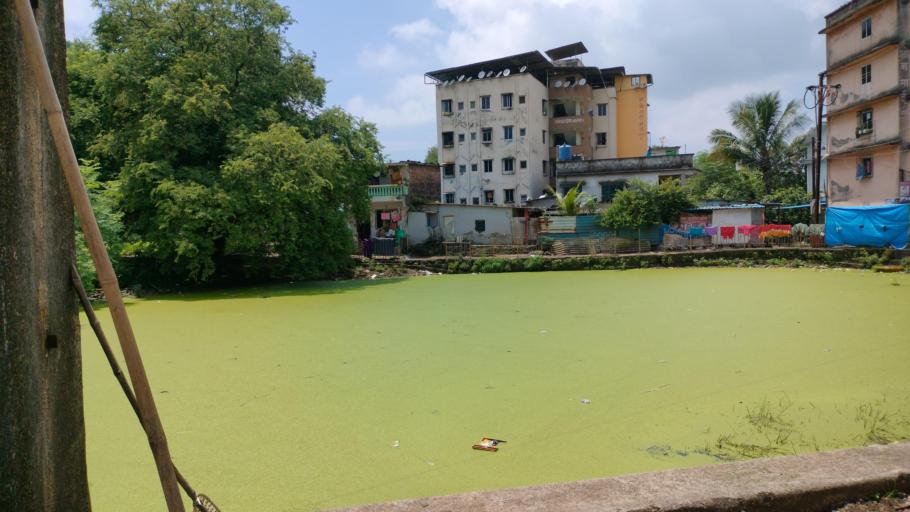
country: IN
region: Maharashtra
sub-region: Thane
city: Virar
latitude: 19.4787
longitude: 72.8206
